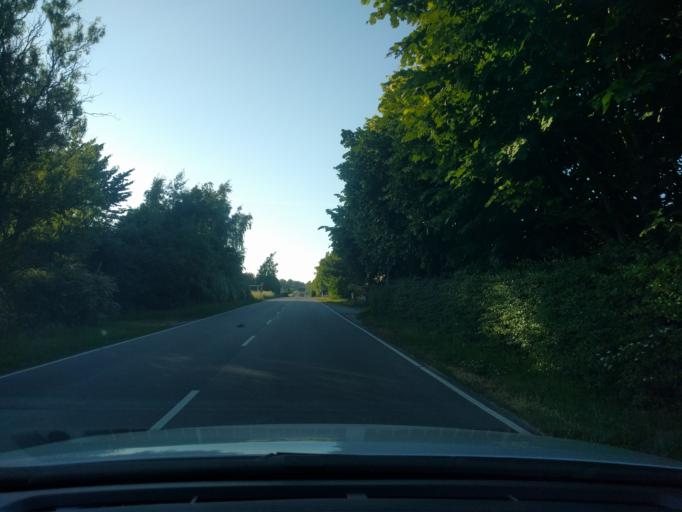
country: DK
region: South Denmark
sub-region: Kerteminde Kommune
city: Kerteminde
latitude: 55.5410
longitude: 10.6612
